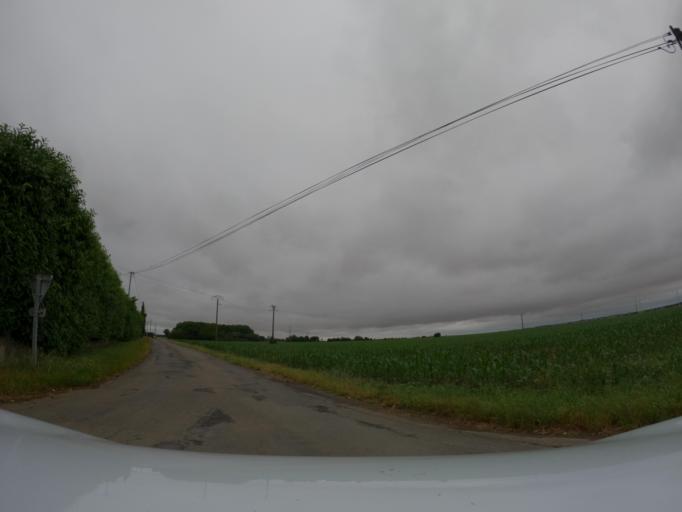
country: FR
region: Pays de la Loire
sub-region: Departement de la Vendee
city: Maillezais
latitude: 46.4183
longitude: -0.7137
